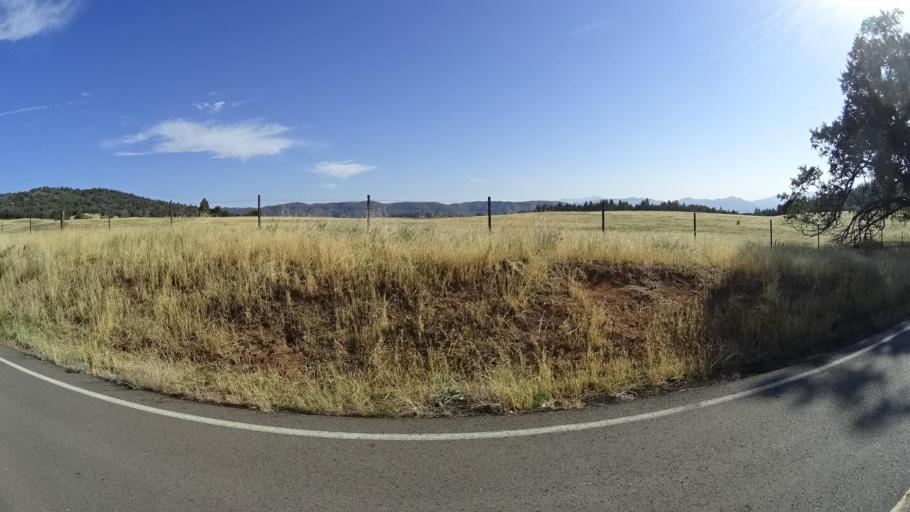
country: US
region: California
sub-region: Riverside County
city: Aguanga
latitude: 33.2886
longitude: -116.8190
